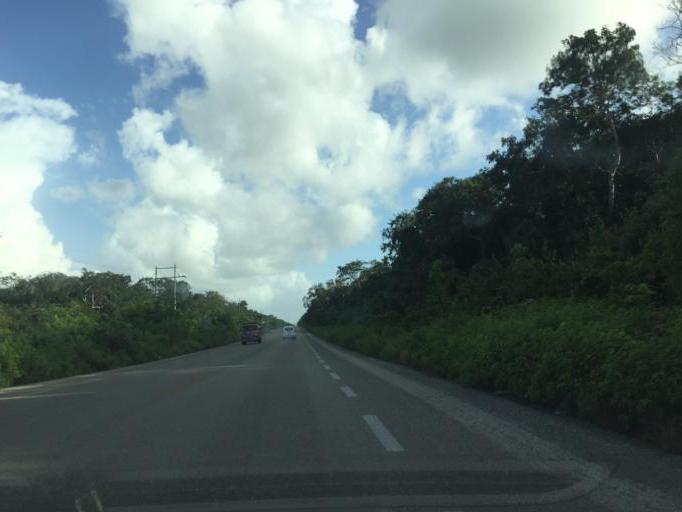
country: MX
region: Quintana Roo
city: Coba
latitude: 20.4627
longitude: -87.6800
